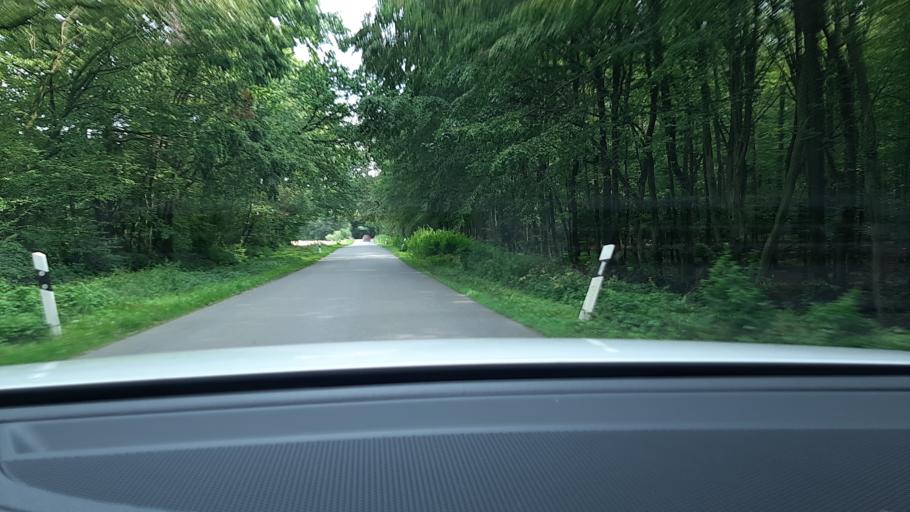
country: DE
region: Schleswig-Holstein
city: Rehhorst
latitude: 53.8552
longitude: 10.4701
